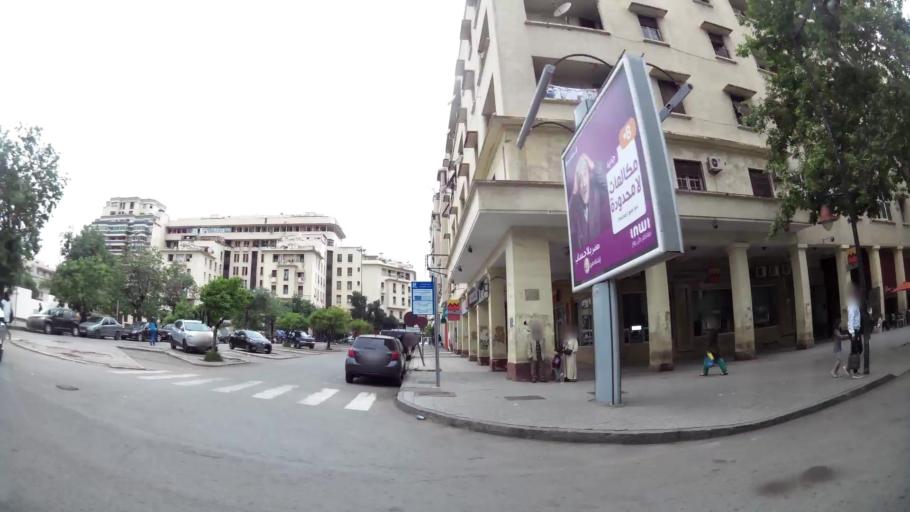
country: MA
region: Fes-Boulemane
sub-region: Fes
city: Fes
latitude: 34.0424
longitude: -4.9991
